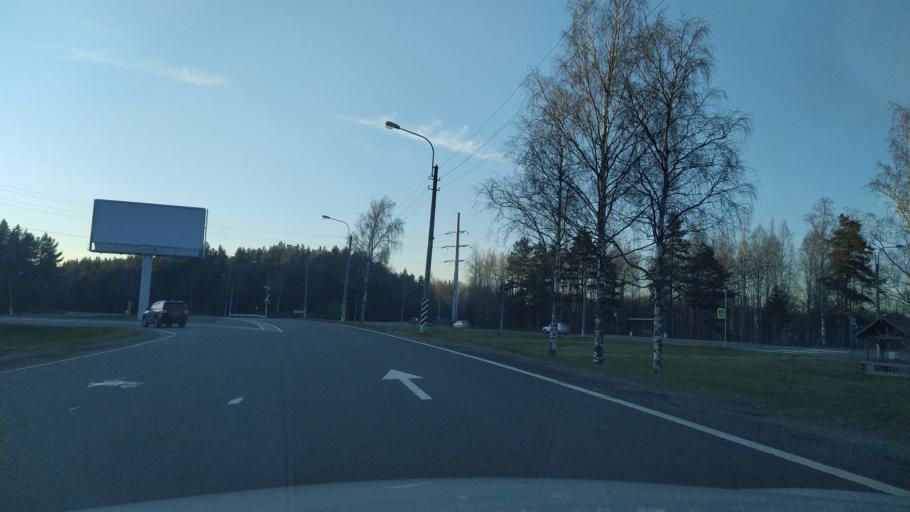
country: RU
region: St.-Petersburg
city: Beloostrov
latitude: 60.1326
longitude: 29.9877
